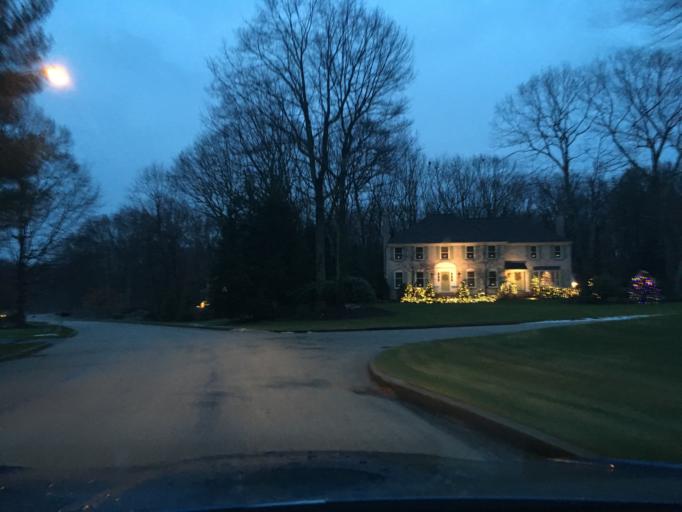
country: US
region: Rhode Island
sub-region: Kent County
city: West Warwick
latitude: 41.6537
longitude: -71.5143
